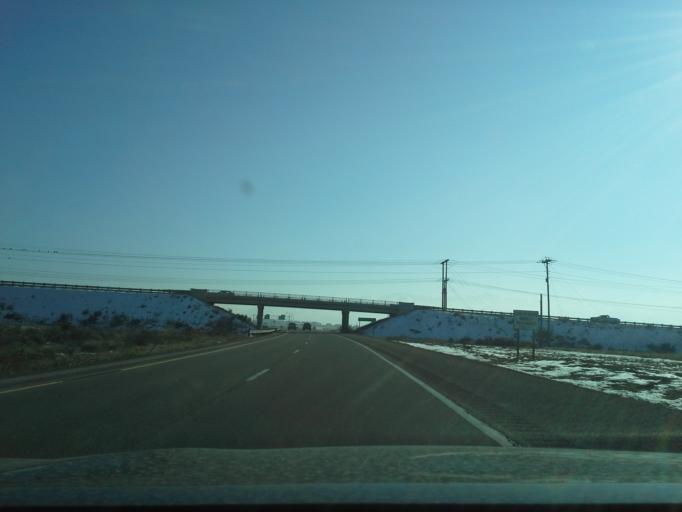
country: US
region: Idaho
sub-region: Bannock County
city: Chubbuck
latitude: 42.9218
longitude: -112.4418
